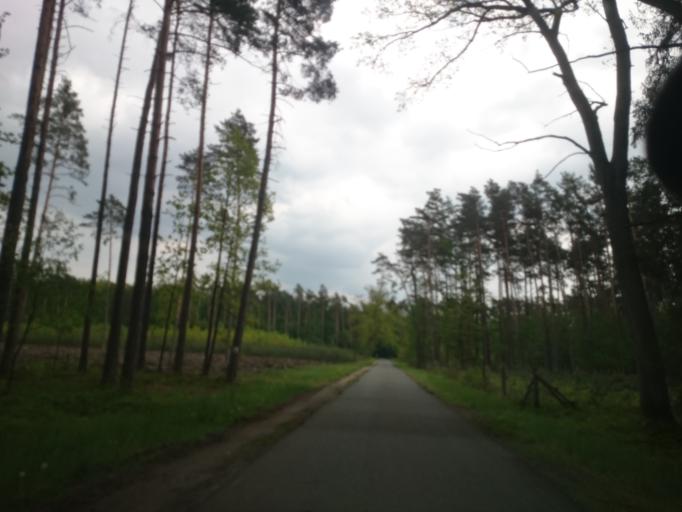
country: PL
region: Lower Silesian Voivodeship
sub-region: Powiat milicki
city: Krosnice
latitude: 51.3888
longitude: 17.3105
